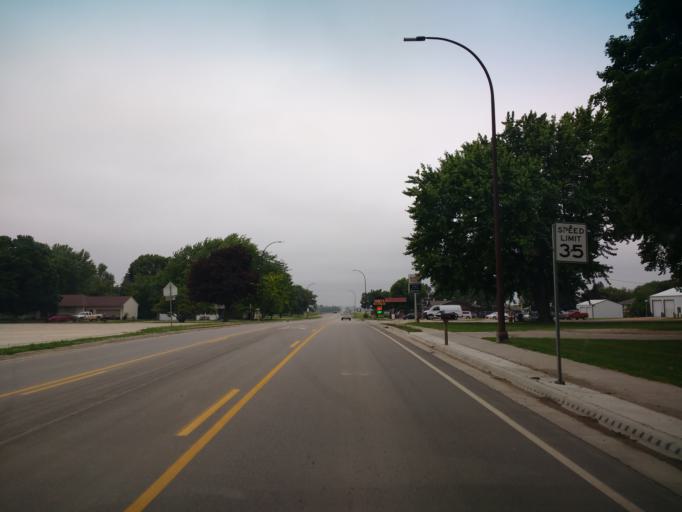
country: US
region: Iowa
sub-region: O'Brien County
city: Sanborn
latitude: 43.1861
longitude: -95.6603
